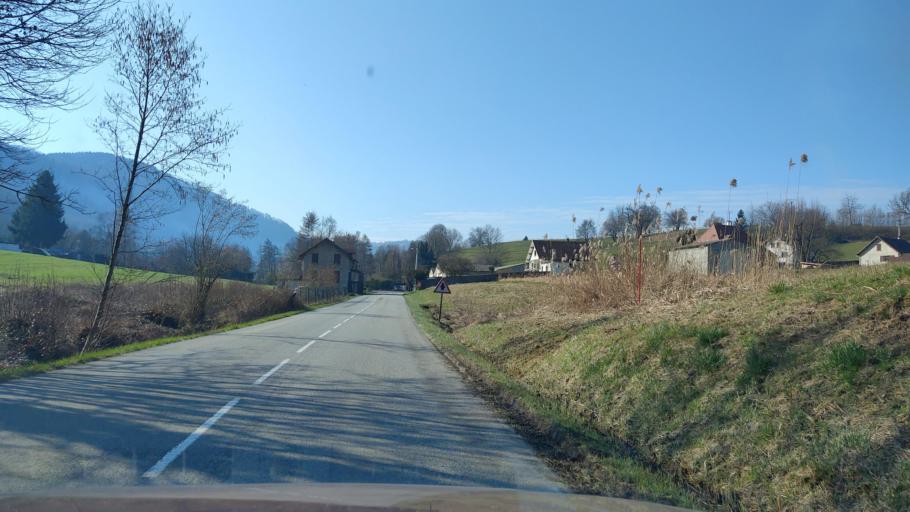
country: FR
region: Rhone-Alpes
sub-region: Departement de la Savoie
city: Saint-Beron
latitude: 45.5120
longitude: 5.7366
